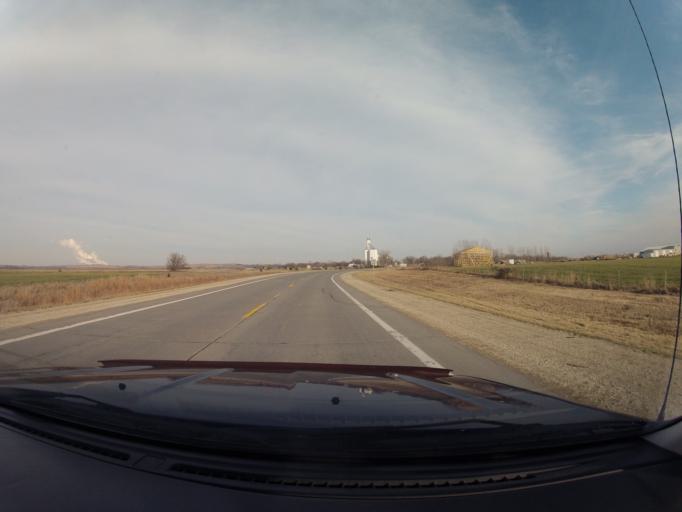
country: US
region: Kansas
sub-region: Pottawatomie County
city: Wamego
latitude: 39.2155
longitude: -96.1913
